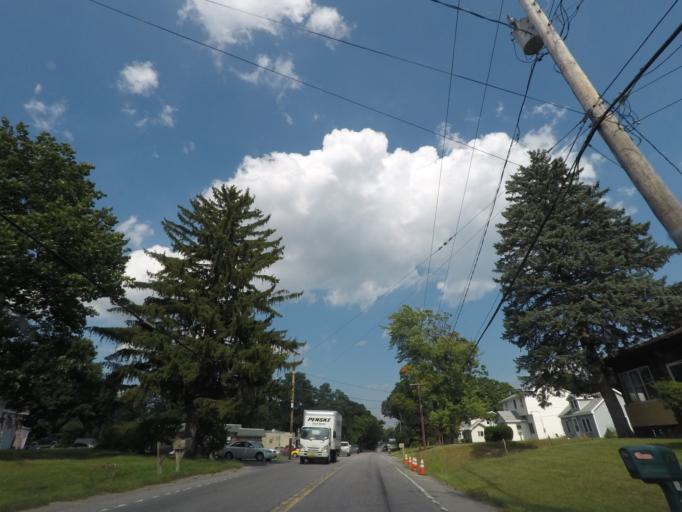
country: US
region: New York
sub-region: Saratoga County
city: Waterford
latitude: 42.7950
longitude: -73.6466
